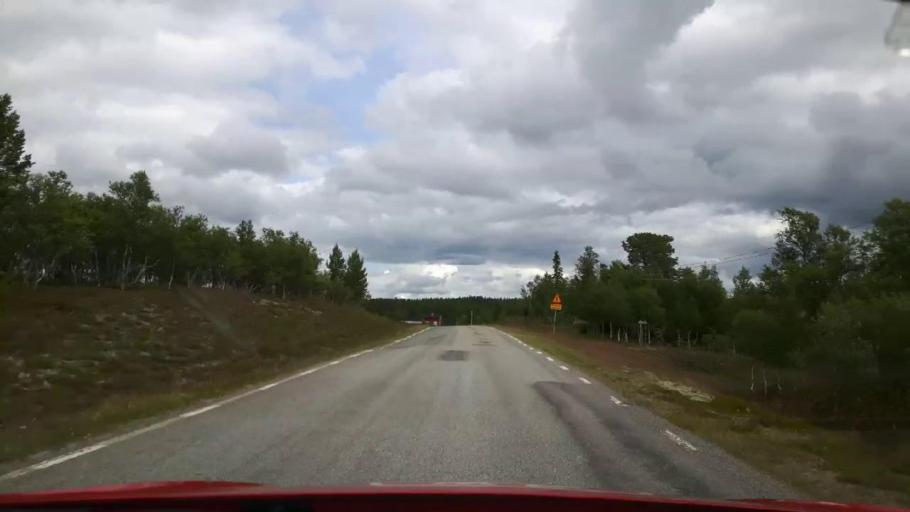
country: NO
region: Hedmark
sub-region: Engerdal
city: Engerdal
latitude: 62.3058
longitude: 12.8036
